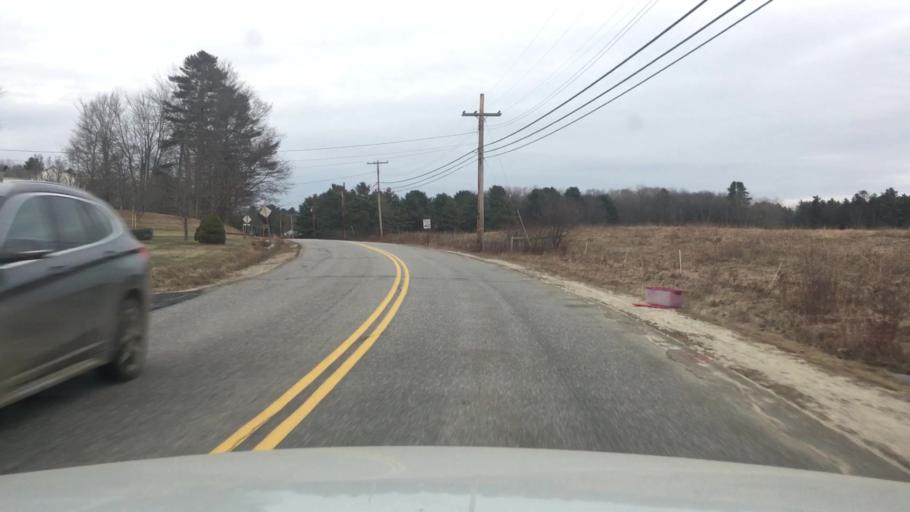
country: US
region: Maine
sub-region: Cumberland County
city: Brunswick
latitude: 43.8899
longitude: -70.0063
